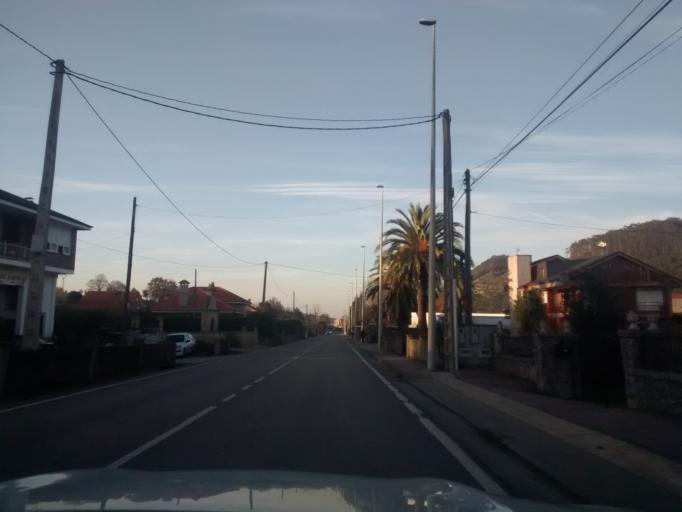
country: ES
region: Cantabria
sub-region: Provincia de Cantabria
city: Entrambasaguas
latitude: 43.3744
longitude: -3.7184
